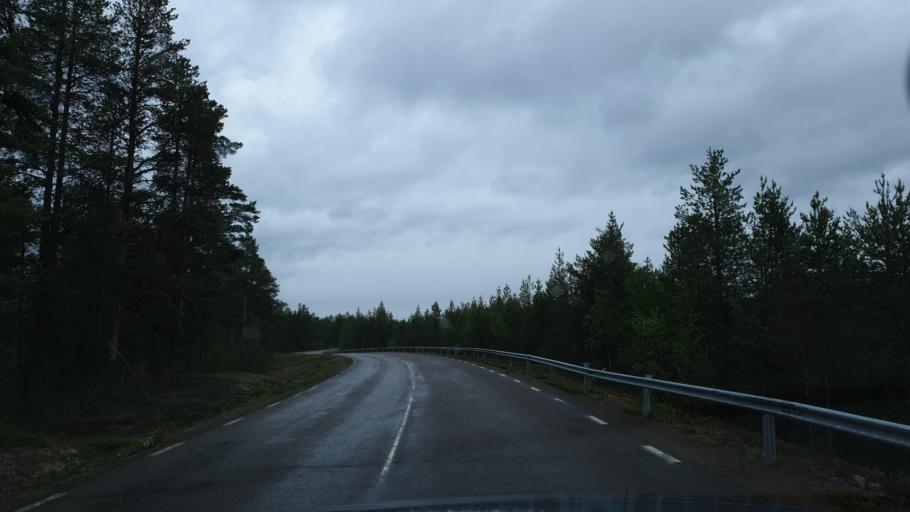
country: SE
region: Norrbotten
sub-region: Kiruna Kommun
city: Kiruna
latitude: 67.8801
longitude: 20.9951
